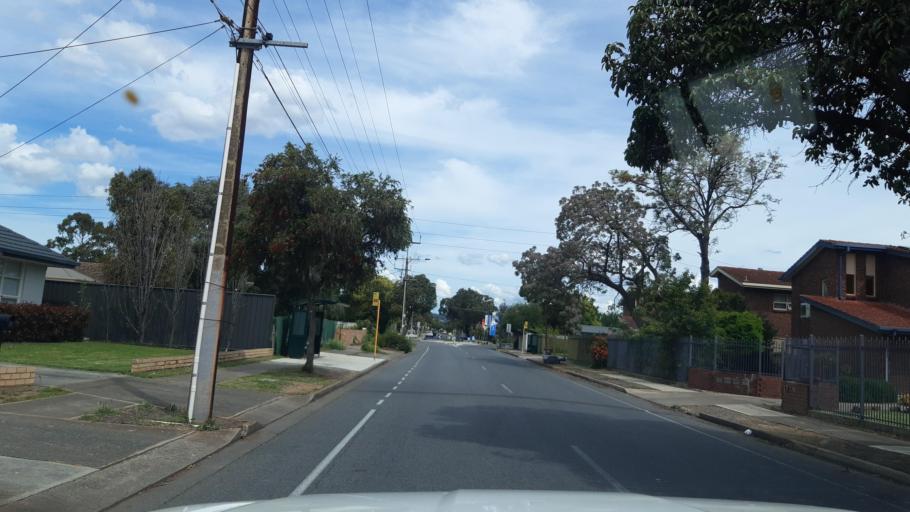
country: AU
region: South Australia
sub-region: Marion
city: Plympton Park
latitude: -34.9838
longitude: 138.5470
